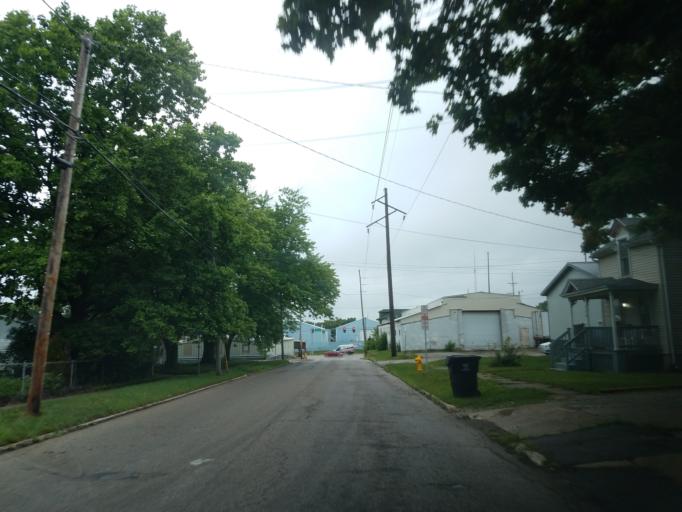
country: US
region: Illinois
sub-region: McLean County
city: Bloomington
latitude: 40.4729
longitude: -88.9819
